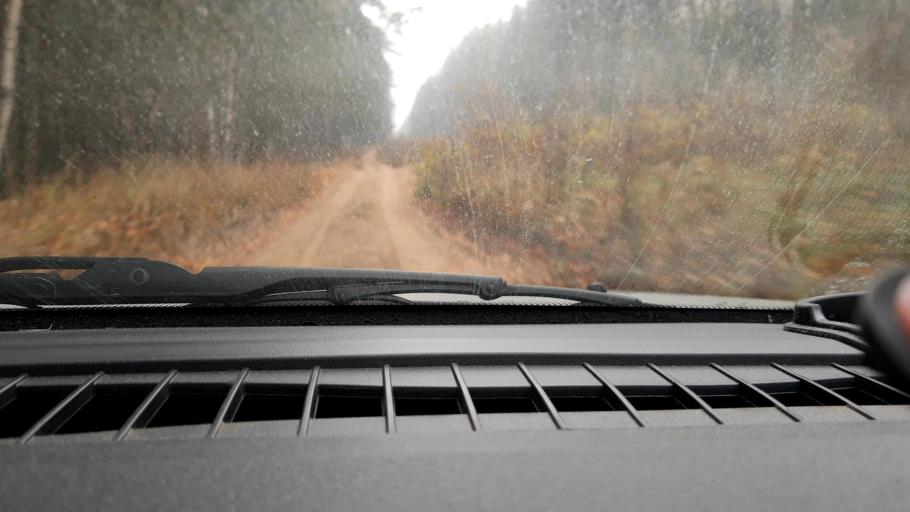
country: RU
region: Nizjnij Novgorod
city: Sitniki
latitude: 56.4271
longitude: 44.0568
